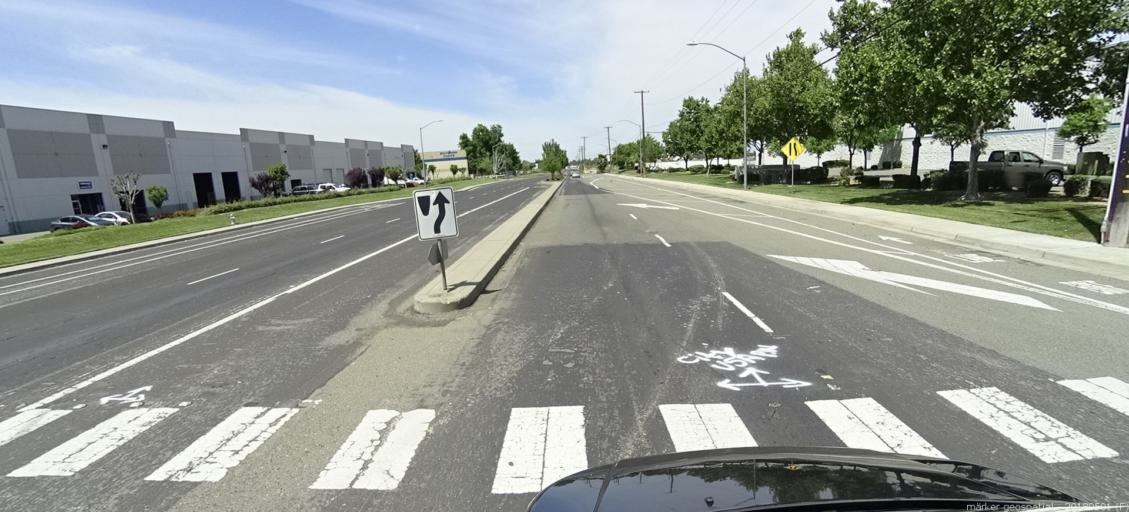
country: US
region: California
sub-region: Sacramento County
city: Rio Linda
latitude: 38.6582
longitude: -121.4291
